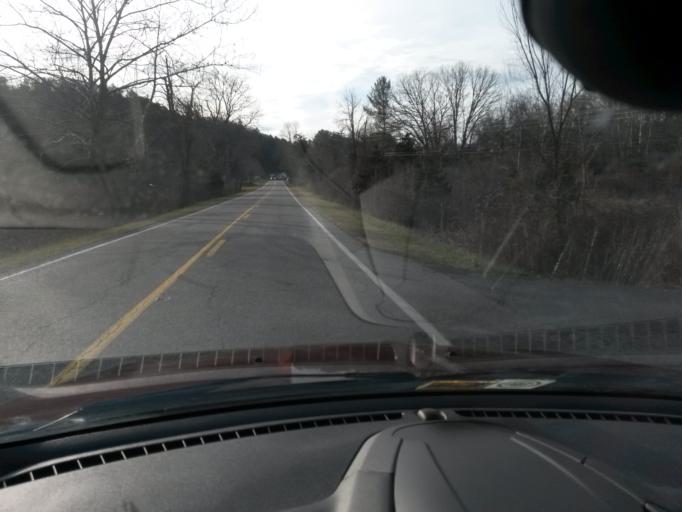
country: US
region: Virginia
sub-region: Bath County
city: Warm Springs
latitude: 37.9934
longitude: -79.6263
